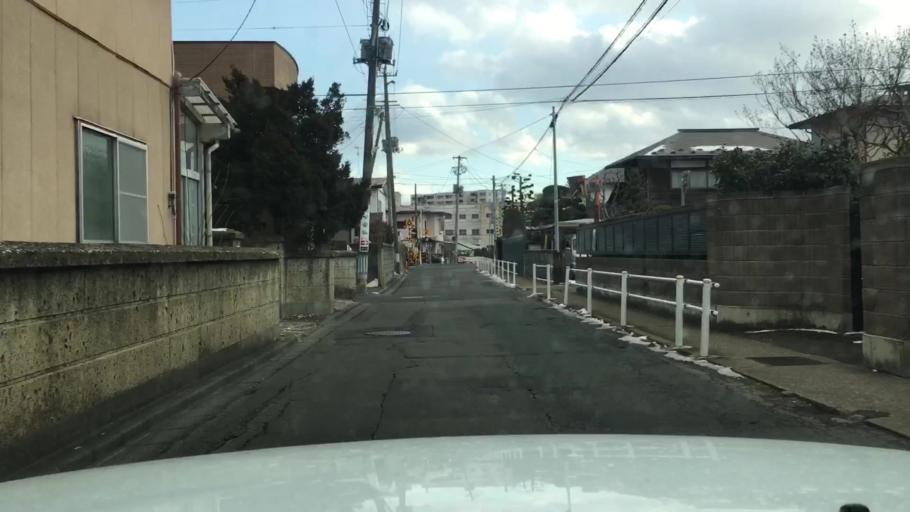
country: JP
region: Iwate
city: Morioka-shi
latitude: 39.7116
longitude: 141.1438
